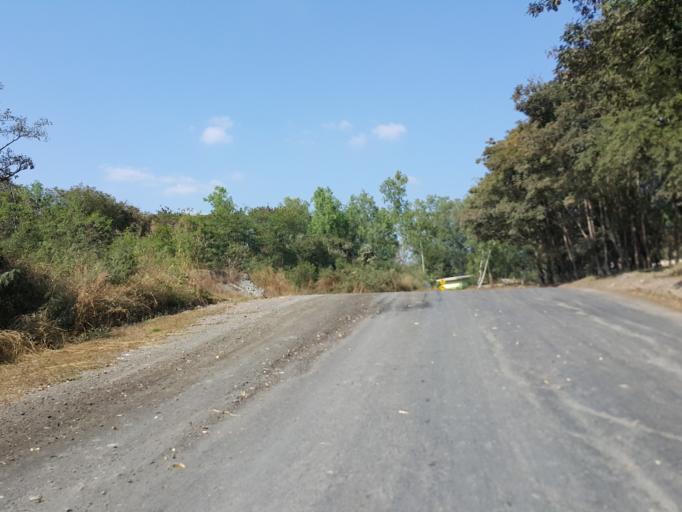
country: TH
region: Chiang Mai
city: Mae On
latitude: 18.8358
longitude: 99.2140
